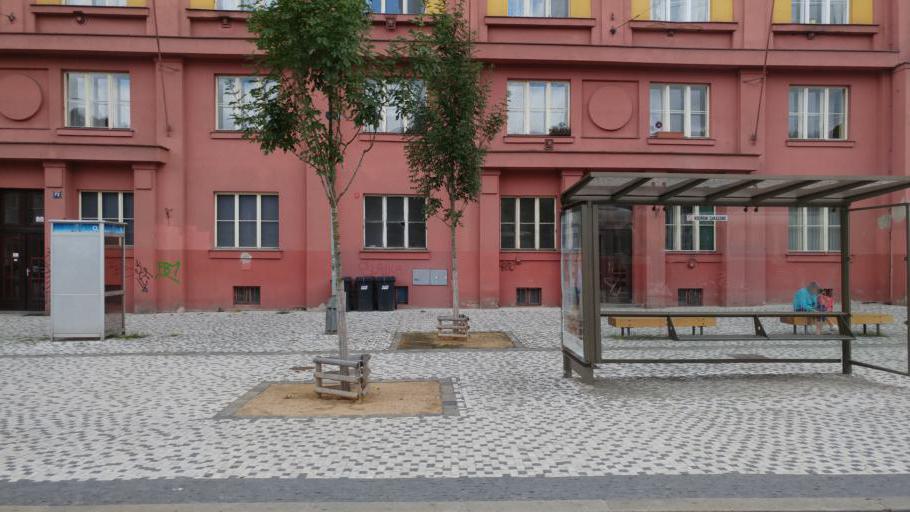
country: CZ
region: Praha
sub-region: Praha 8
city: Karlin
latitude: 50.0681
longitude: 14.4592
